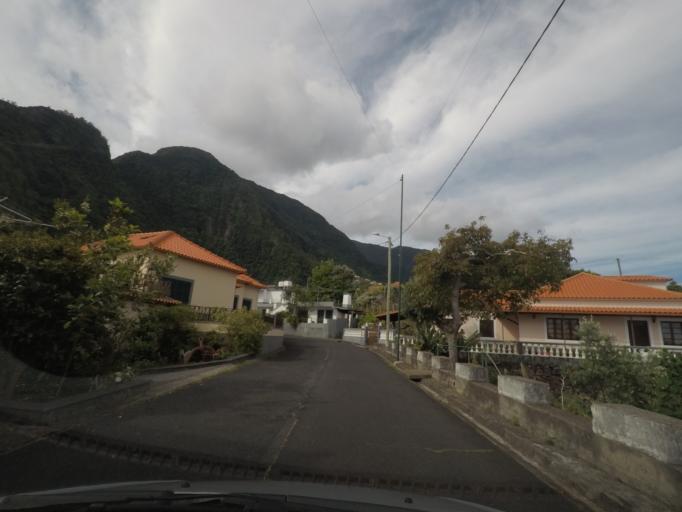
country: PT
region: Madeira
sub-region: Sao Vicente
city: Sao Vicente
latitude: 32.8278
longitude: -16.9885
